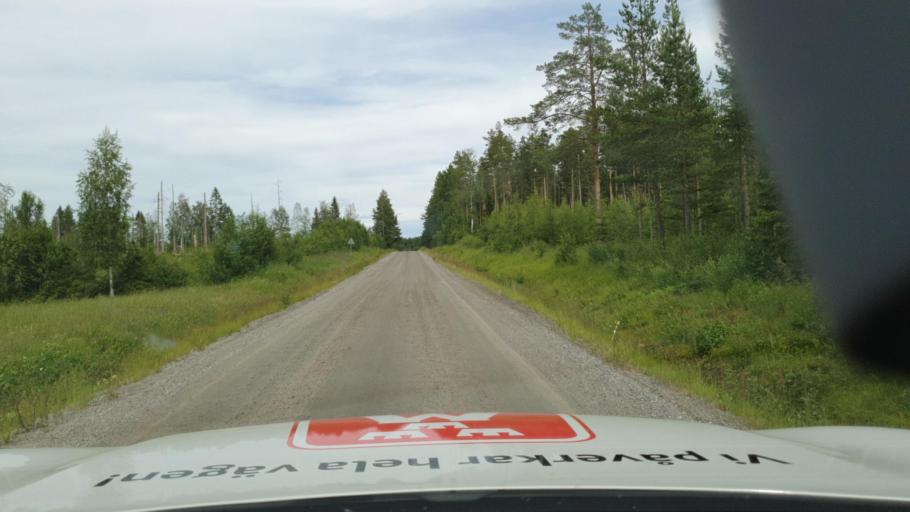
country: SE
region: Vaesterbotten
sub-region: Skelleftea Kommun
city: Viken
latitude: 64.5093
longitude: 20.9322
